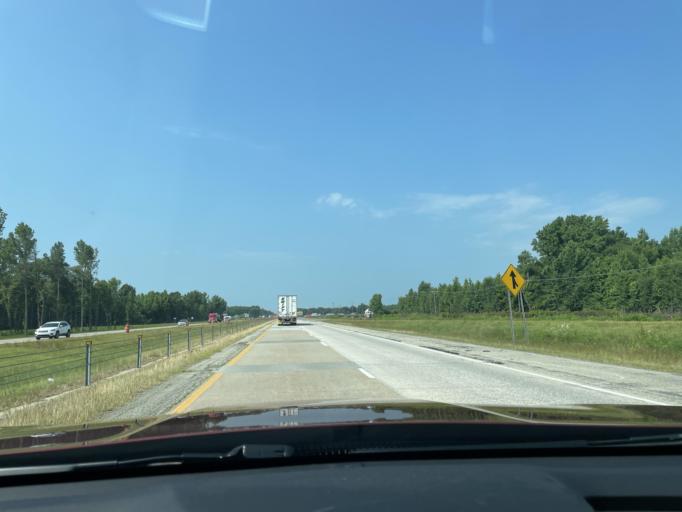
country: US
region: Arkansas
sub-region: White County
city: Searcy
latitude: 35.2028
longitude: -91.7338
